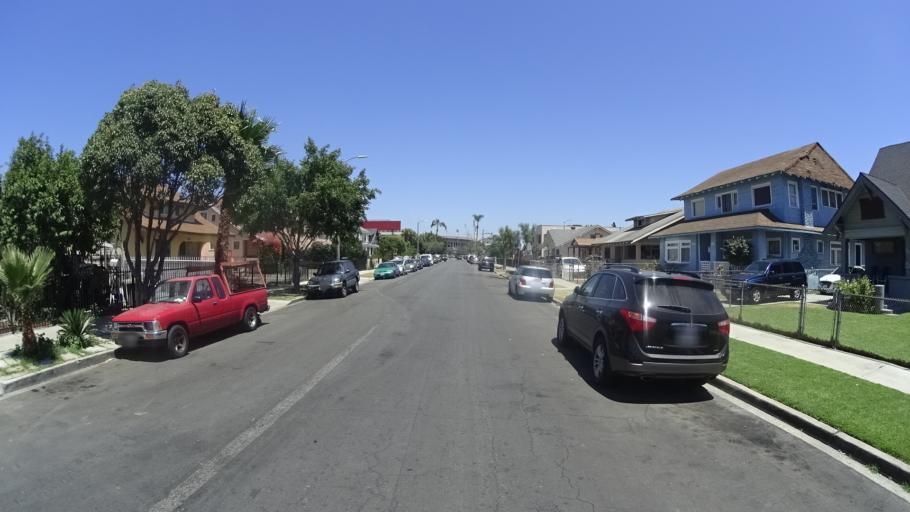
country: US
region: California
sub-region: Los Angeles County
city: View Park-Windsor Hills
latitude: 34.0132
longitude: -118.2946
